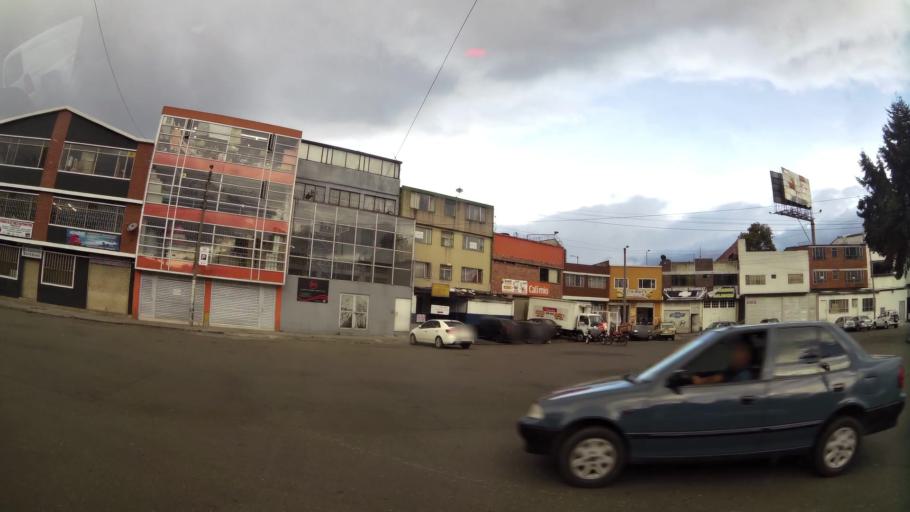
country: CO
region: Bogota D.C.
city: Bogota
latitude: 4.5967
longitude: -74.1147
